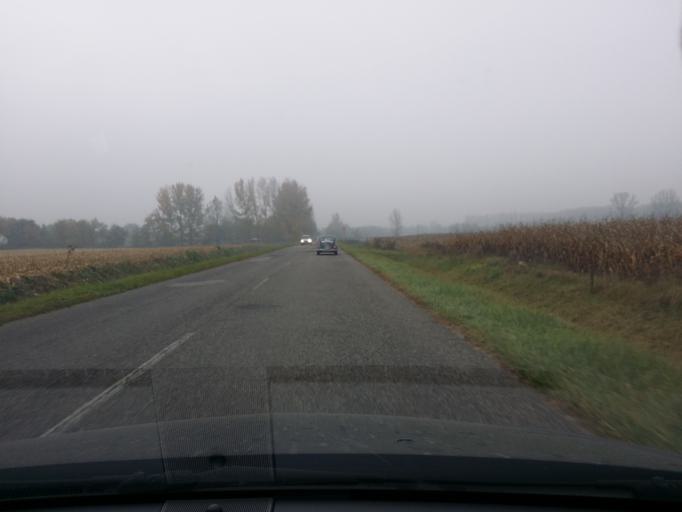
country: HU
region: Szabolcs-Szatmar-Bereg
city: Nyirbogdany
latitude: 48.0569
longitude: 21.8604
